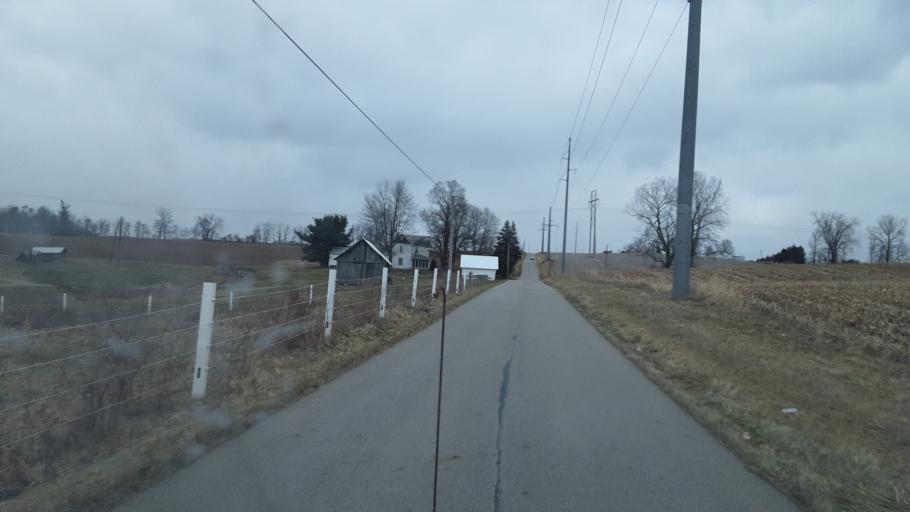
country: US
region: Ohio
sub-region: Perry County
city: Thornport
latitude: 39.9461
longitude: -82.3935
